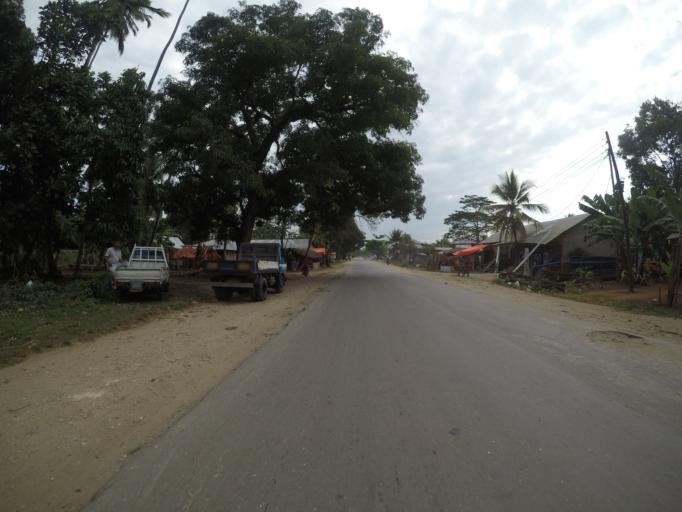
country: TZ
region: Zanzibar Central/South
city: Koani
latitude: -6.1950
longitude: 39.2851
